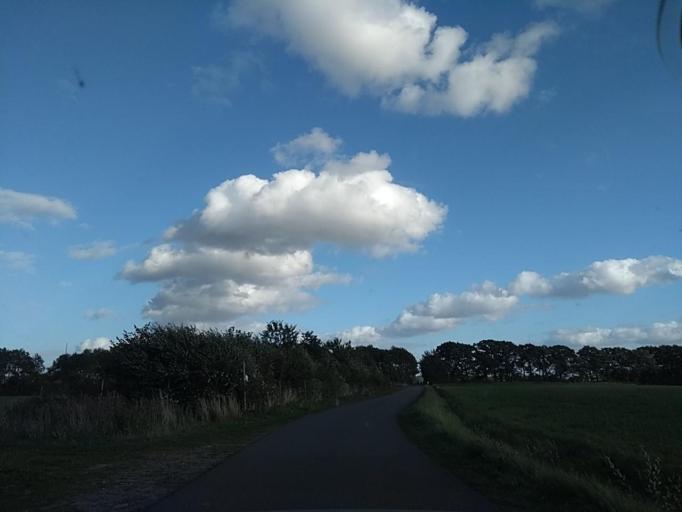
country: DE
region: Mecklenburg-Vorpommern
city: Ostseebad Dierhagen
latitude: 54.2362
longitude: 12.3700
